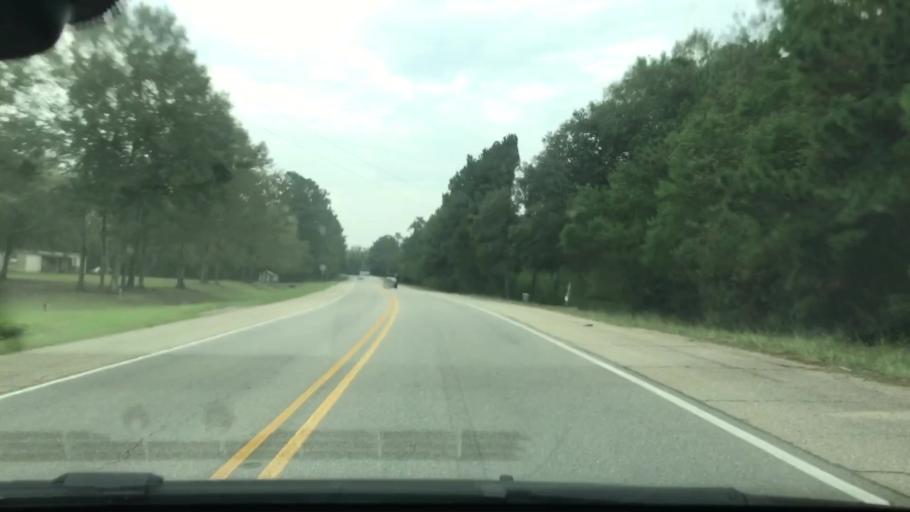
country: US
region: Louisiana
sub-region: Saint Tammany Parish
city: Pearl River
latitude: 30.4251
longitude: -89.7877
